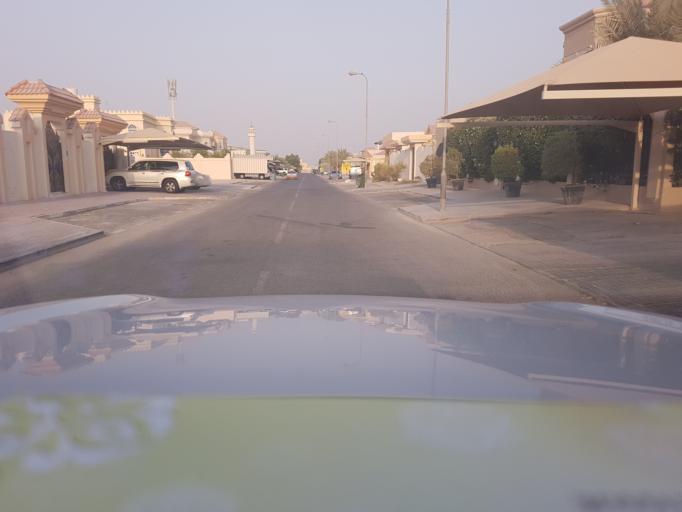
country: QA
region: Baladiyat ad Dawhah
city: Doha
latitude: 25.2327
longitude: 51.5616
